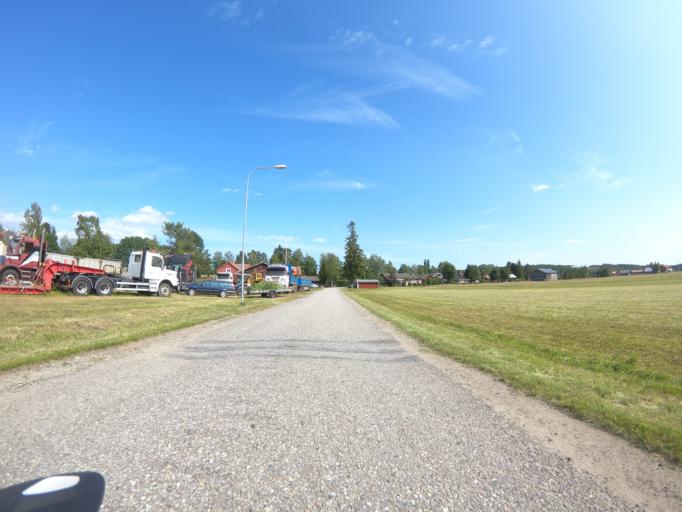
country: SE
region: Vaesterbotten
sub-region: Umea Kommun
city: Roback
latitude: 63.8318
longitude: 20.1204
